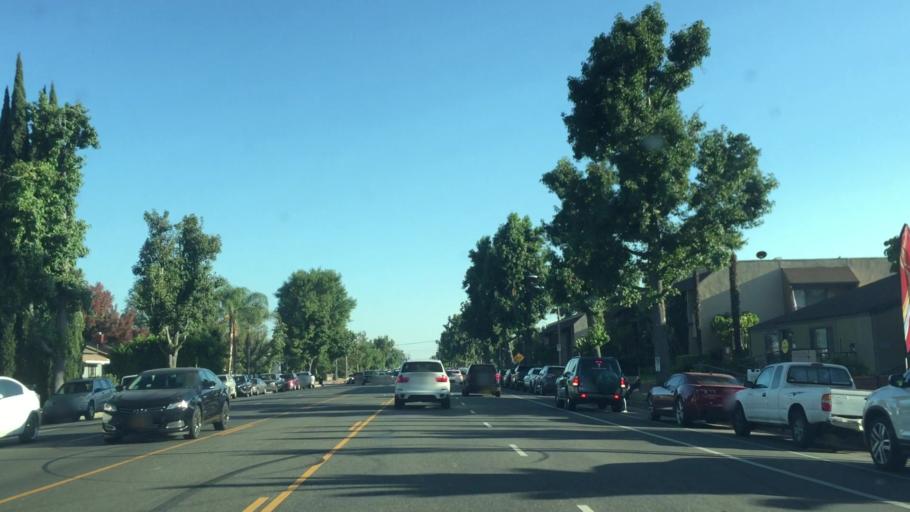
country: US
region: California
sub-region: Los Angeles County
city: San Fernando
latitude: 34.2551
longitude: -118.4850
